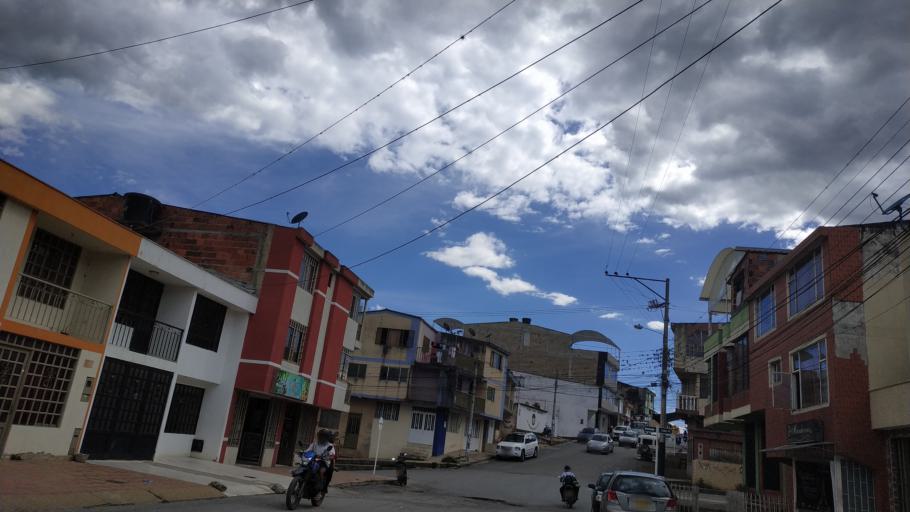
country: CO
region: Santander
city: Barbosa
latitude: 5.9336
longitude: -73.6137
